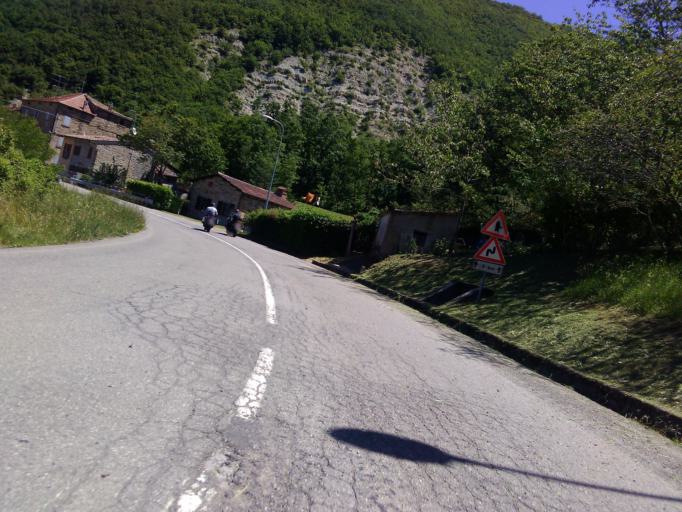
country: IT
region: Emilia-Romagna
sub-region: Provincia di Parma
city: Terenzo
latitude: 44.5667
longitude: 10.0532
